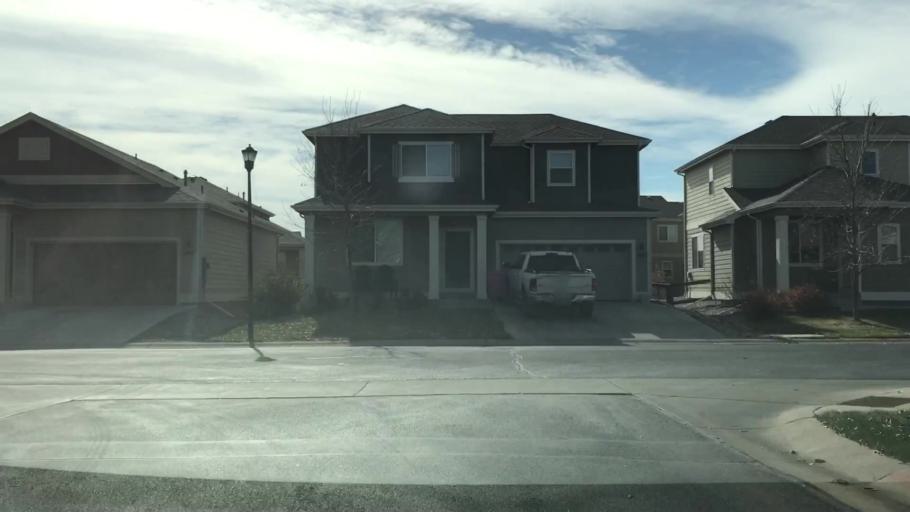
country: US
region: Colorado
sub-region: Larimer County
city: Fort Collins
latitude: 40.5938
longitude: -105.0430
